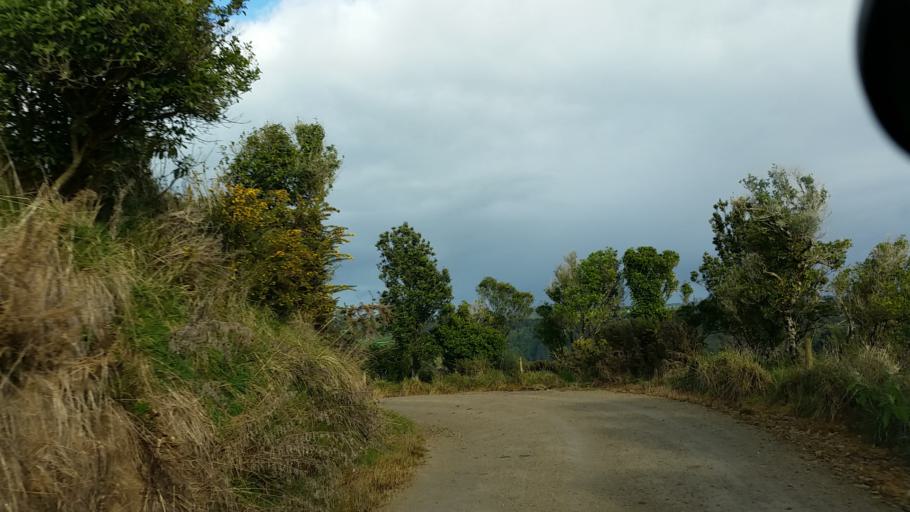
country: NZ
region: Taranaki
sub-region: South Taranaki District
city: Patea
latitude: -39.7257
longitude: 174.7132
